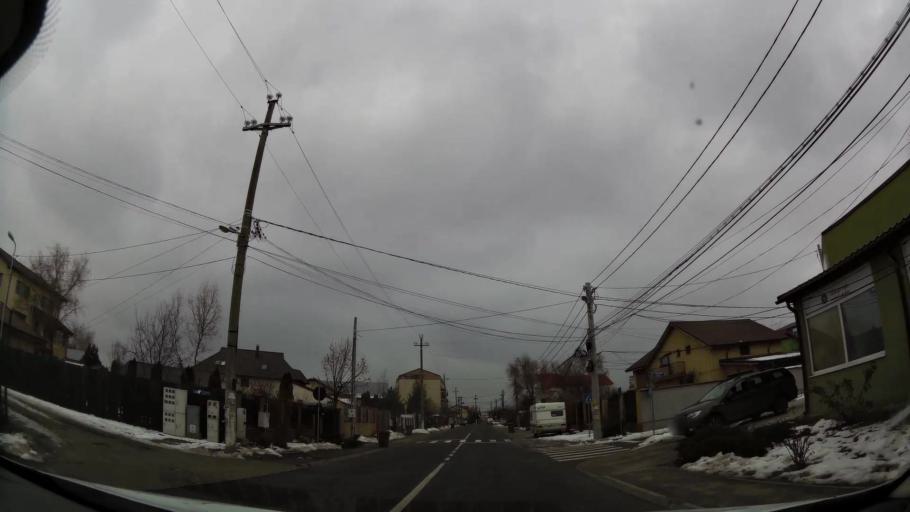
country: RO
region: Ilfov
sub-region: Comuna Otopeni
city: Otopeni
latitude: 44.5534
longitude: 26.0801
